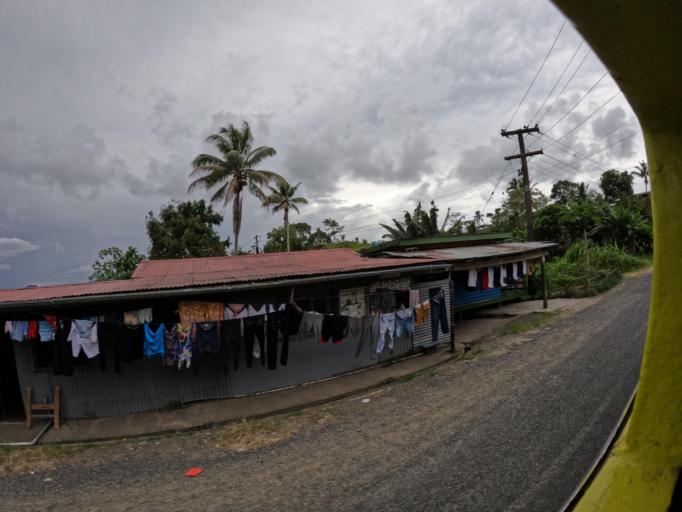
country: FJ
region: Central
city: Suva
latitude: -18.0785
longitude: 178.4585
